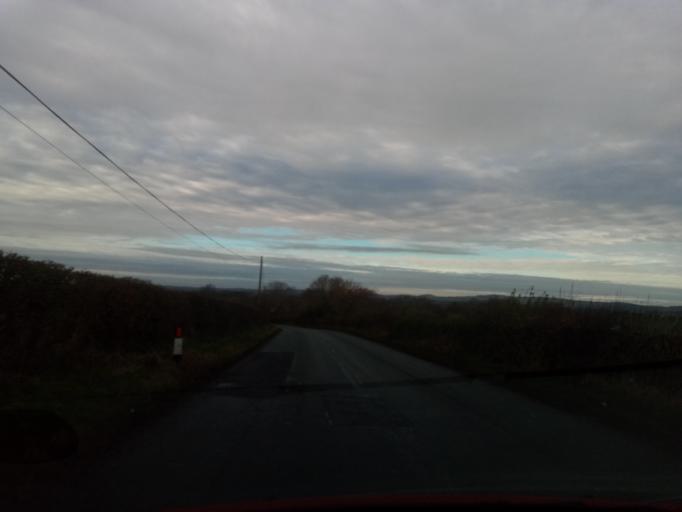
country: GB
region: Scotland
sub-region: The Scottish Borders
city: Coldstream
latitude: 55.7184
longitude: -2.2496
